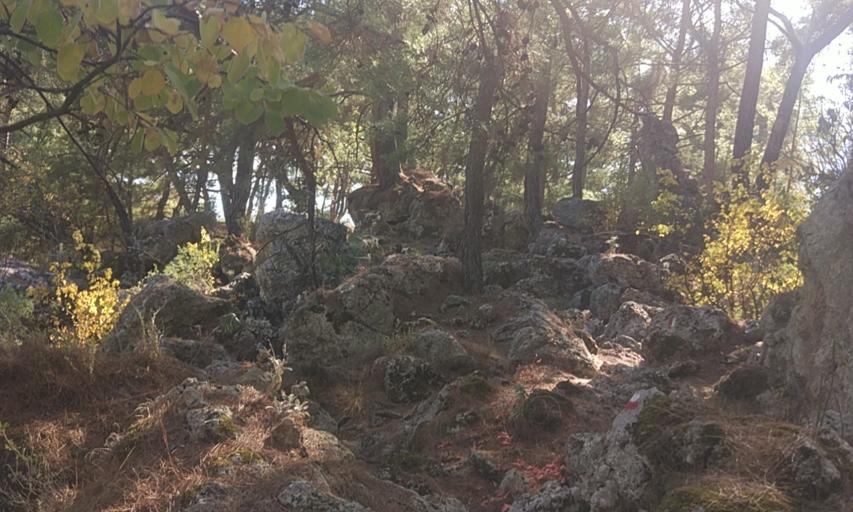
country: TR
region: Antalya
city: Tekirova
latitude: 36.4892
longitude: 30.4277
